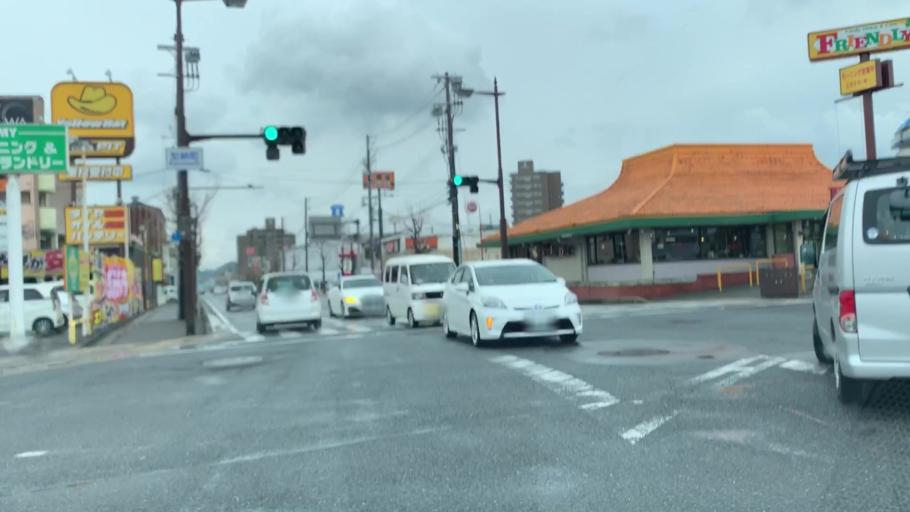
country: JP
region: Wakayama
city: Wakayama-shi
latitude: 34.2246
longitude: 135.1596
